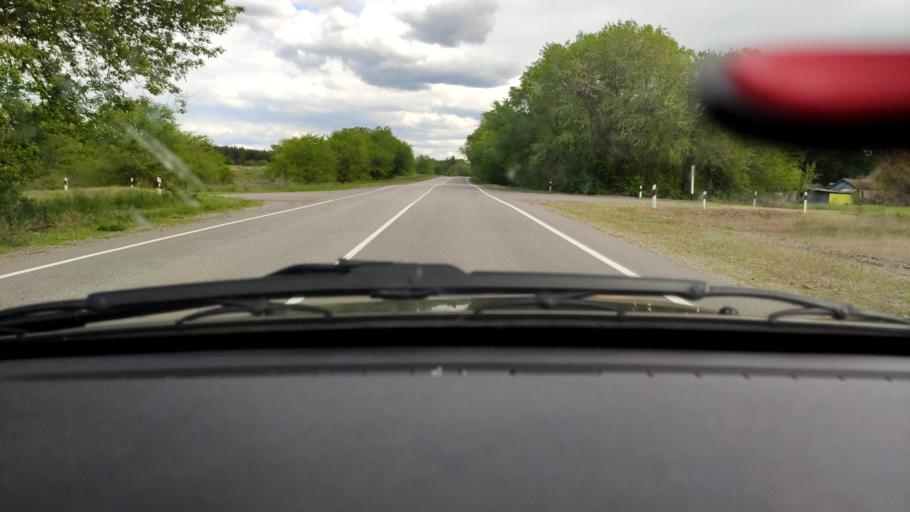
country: RU
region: Voronezj
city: Ostrogozhsk
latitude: 51.0551
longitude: 38.9242
